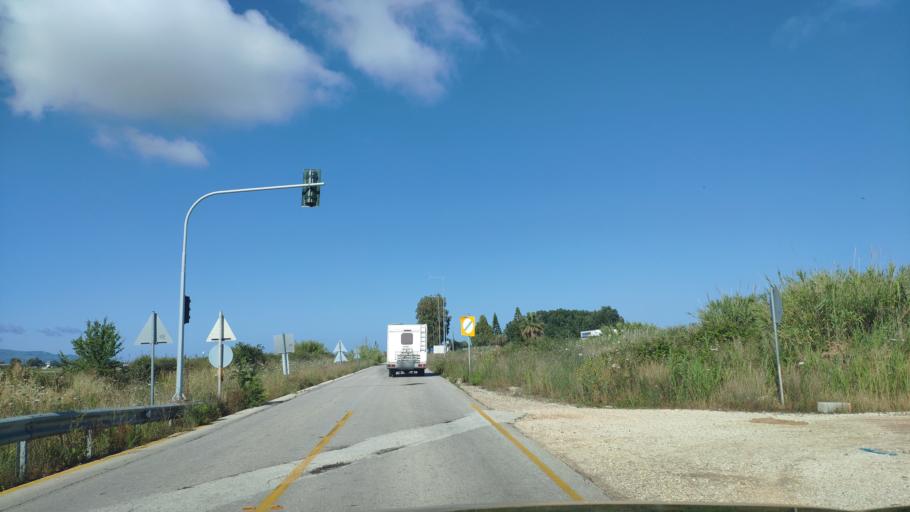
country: GR
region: Epirus
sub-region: Nomos Prevezis
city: Preveza
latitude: 38.9319
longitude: 20.7801
